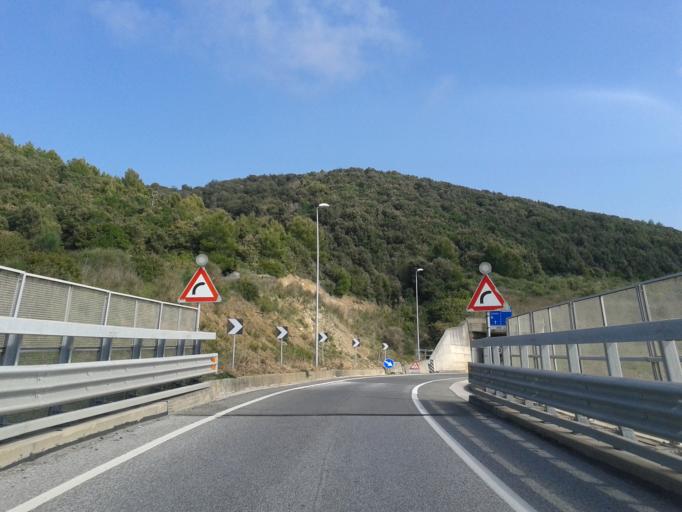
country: IT
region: Tuscany
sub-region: Provincia di Livorno
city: Quercianella
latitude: 43.4835
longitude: 10.3346
